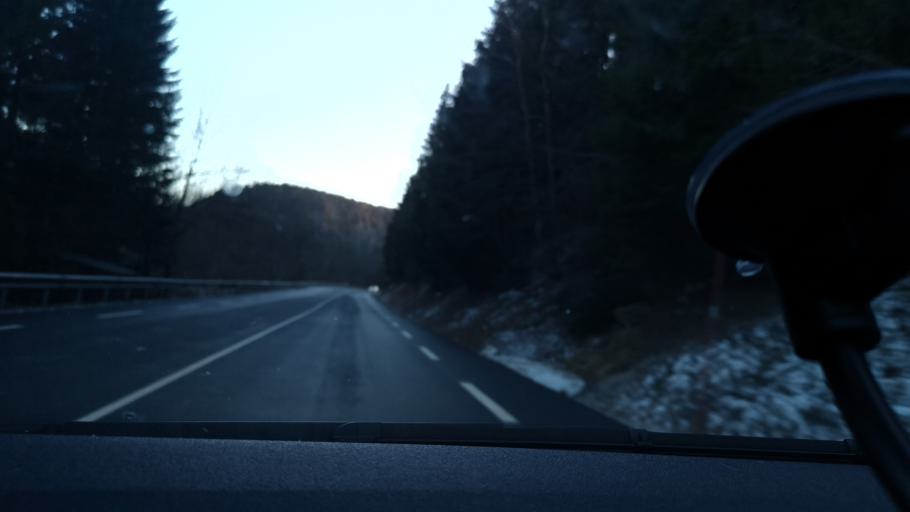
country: FR
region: Franche-Comte
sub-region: Departement du Doubs
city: La Cluse-et-Mijoux
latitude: 46.8715
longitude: 6.3646
